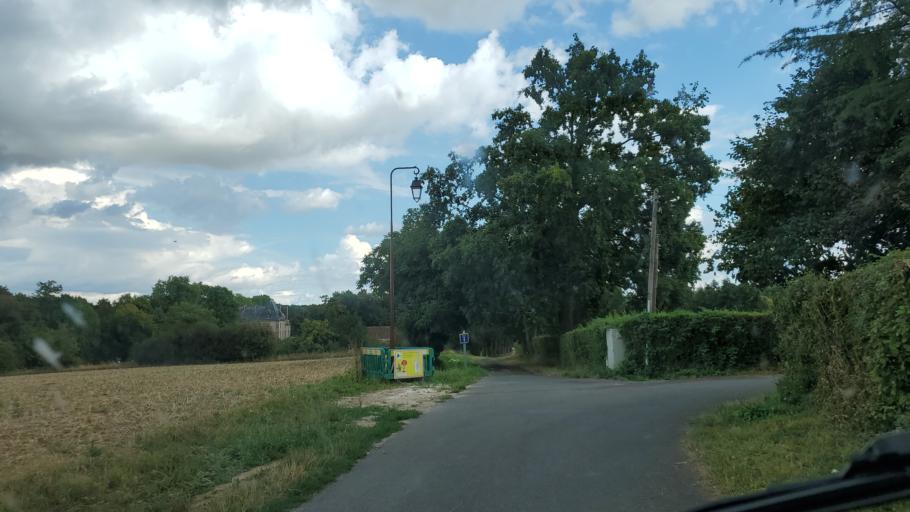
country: FR
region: Ile-de-France
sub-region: Departement de Seine-et-Marne
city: Chailly-en-Brie
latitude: 48.7771
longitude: 3.1667
